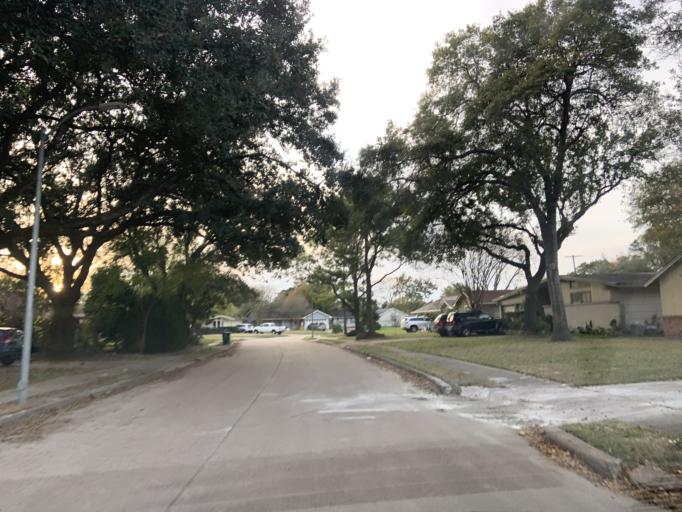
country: US
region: Texas
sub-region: Harris County
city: Bellaire
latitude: 29.6932
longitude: -95.5083
